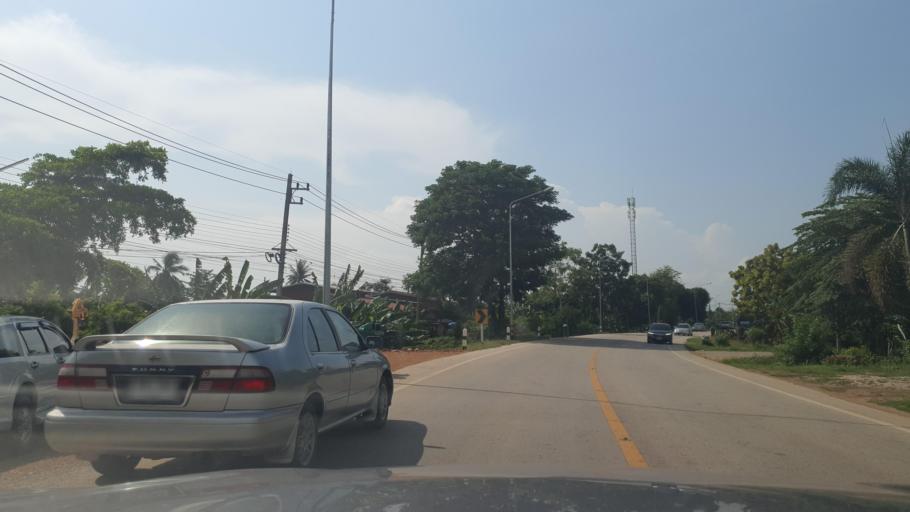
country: TH
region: Sukhothai
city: Si Samrong
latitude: 17.1974
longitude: 99.8488
